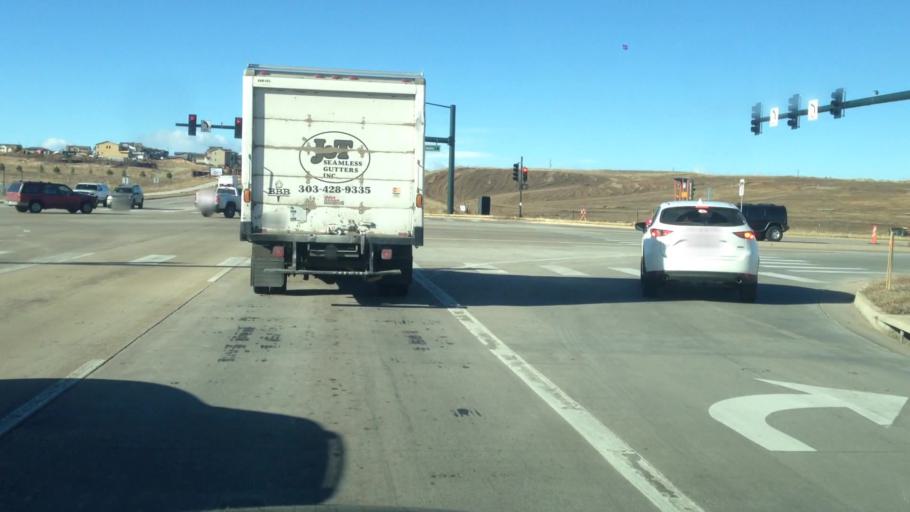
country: US
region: Colorado
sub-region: Douglas County
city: Stonegate
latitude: 39.5172
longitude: -104.8127
